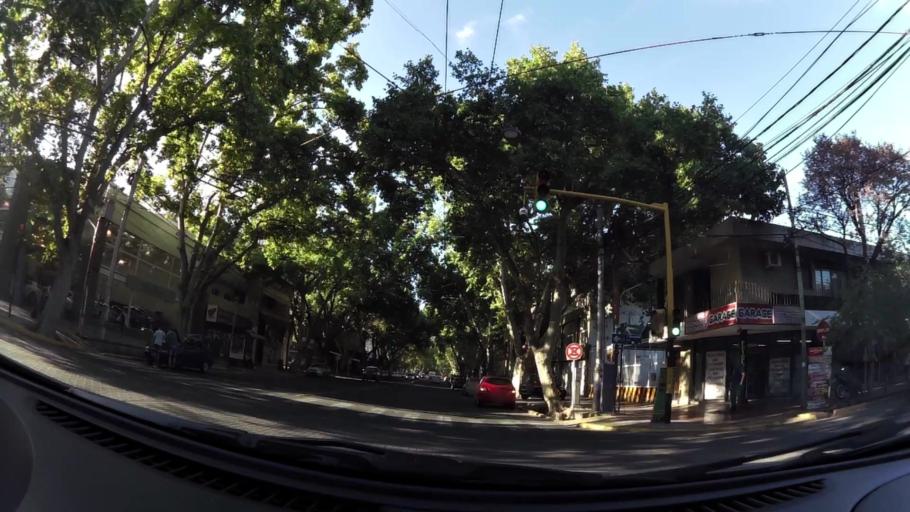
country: AR
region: Mendoza
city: Mendoza
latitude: -32.9013
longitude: -68.8421
